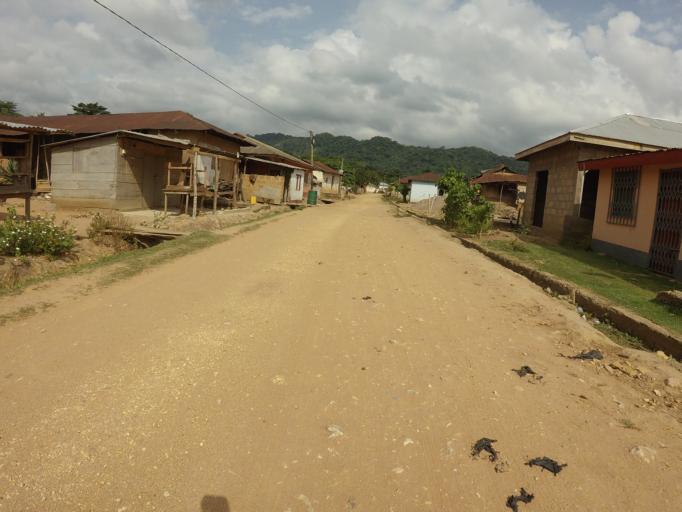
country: GH
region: Volta
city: Kpandu
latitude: 6.8944
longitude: 0.4322
